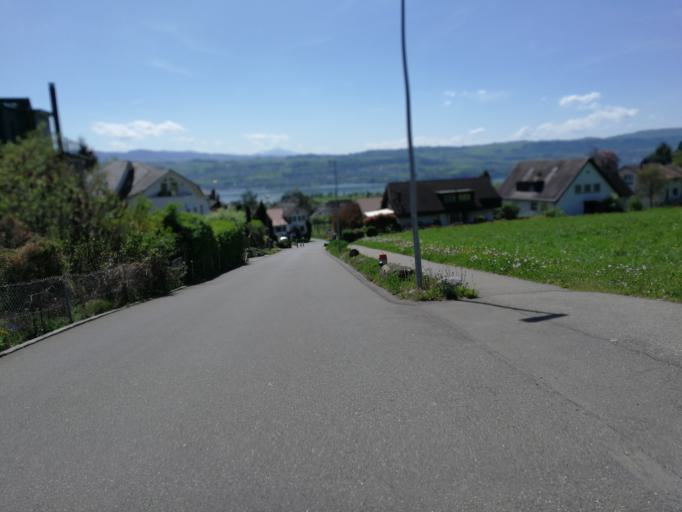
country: CH
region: Zurich
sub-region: Bezirk Meilen
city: Uetikon / Grossdorf
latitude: 47.2697
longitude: 8.6803
